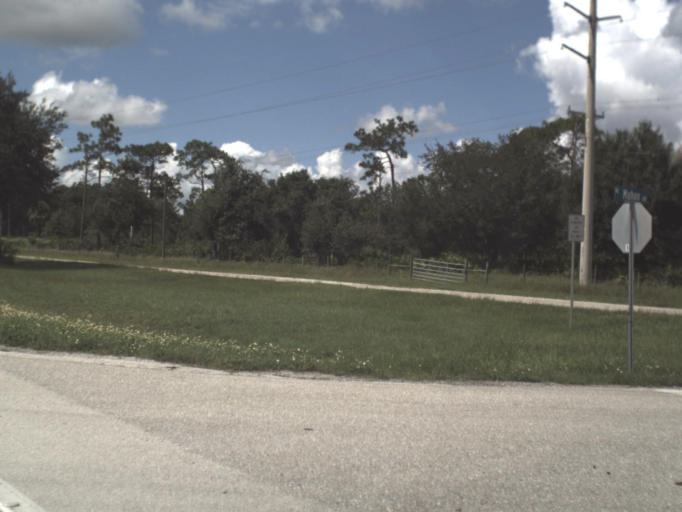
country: US
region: Florida
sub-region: DeSoto County
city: Southeast Arcadia
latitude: 27.2088
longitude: -81.7617
